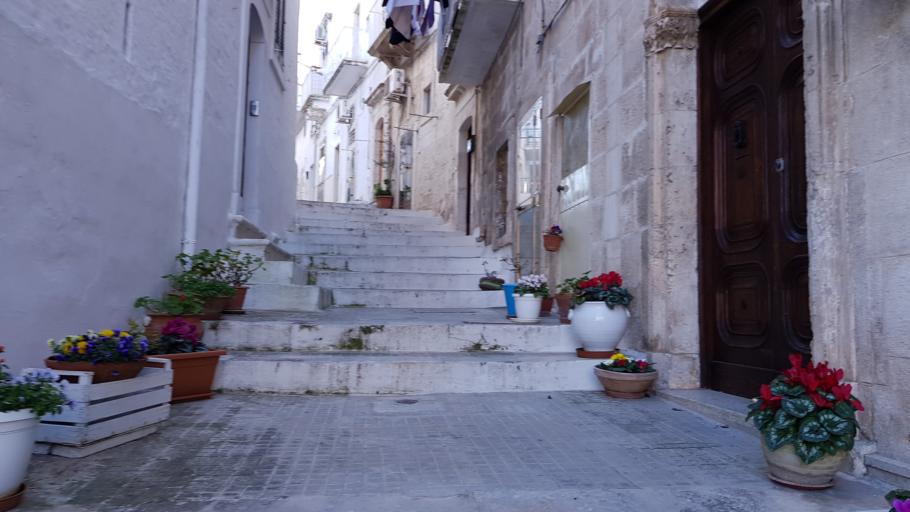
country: IT
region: Apulia
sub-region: Provincia di Brindisi
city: Ostuni
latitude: 40.7295
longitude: 17.5810
